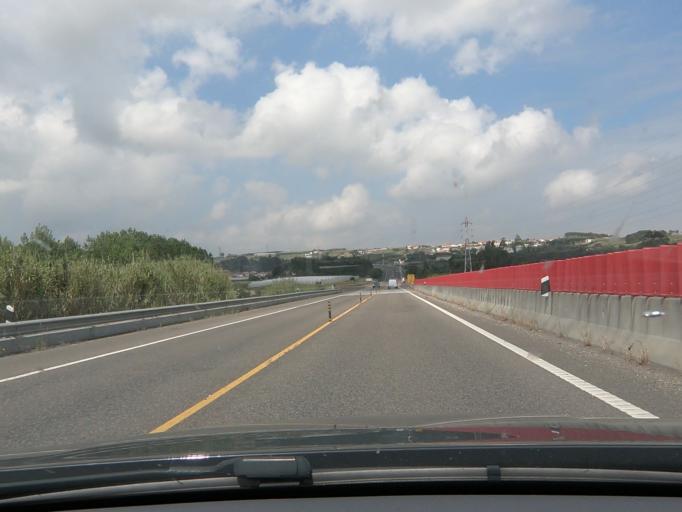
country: PT
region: Leiria
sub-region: Obidos
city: Obidos
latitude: 39.3370
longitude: -9.2212
